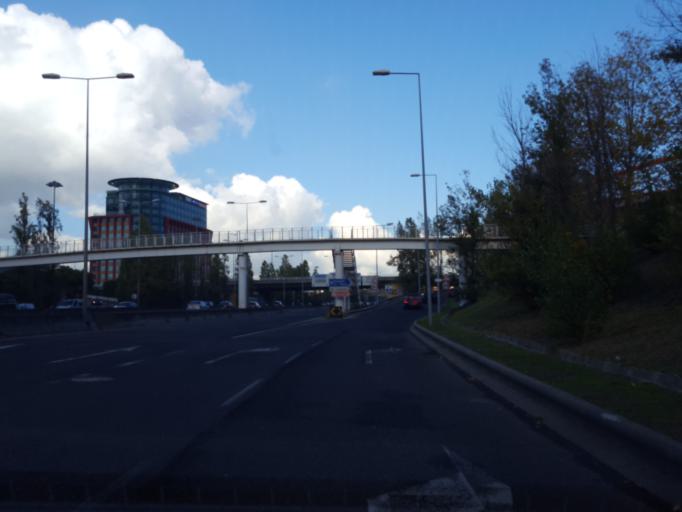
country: PT
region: Lisbon
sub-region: Odivelas
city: Pontinha
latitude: 38.7507
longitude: -9.1882
